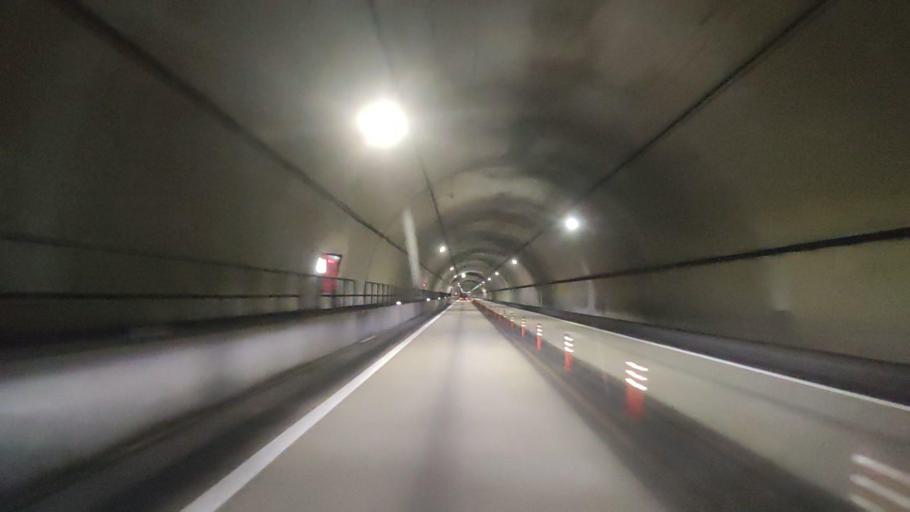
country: JP
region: Wakayama
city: Tanabe
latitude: 33.5448
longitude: 135.5235
